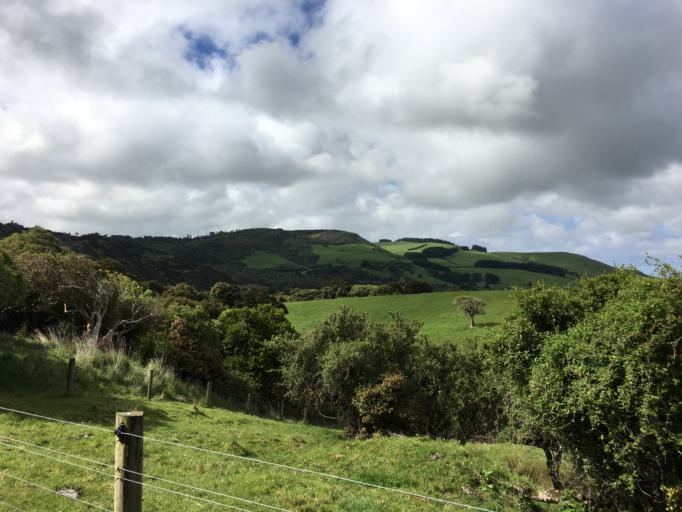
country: NZ
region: Otago
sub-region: Clutha District
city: Papatowai
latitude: -46.4969
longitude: 169.4764
